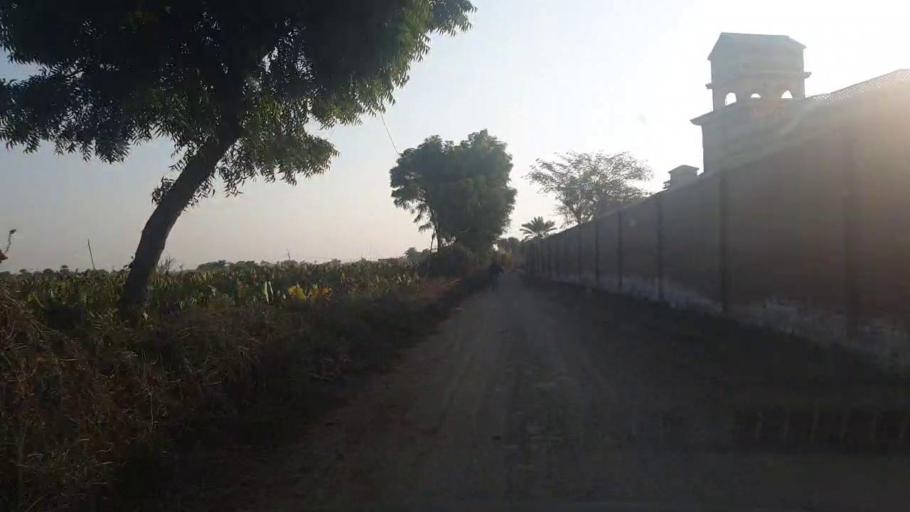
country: PK
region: Sindh
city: Sakrand
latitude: 26.0979
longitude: 68.3975
